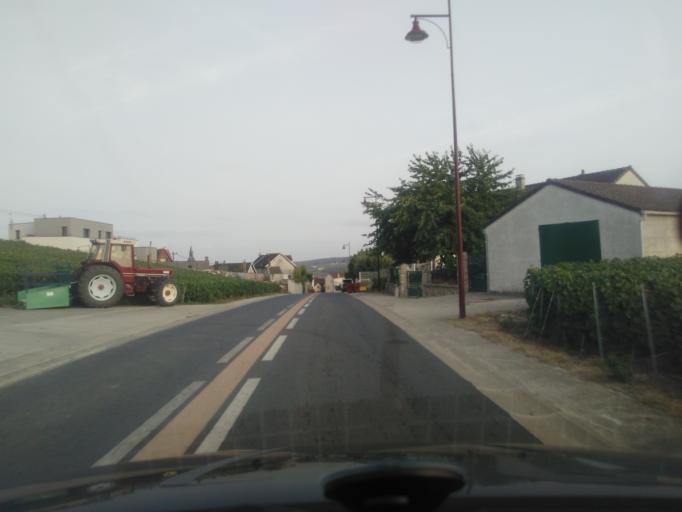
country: FR
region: Champagne-Ardenne
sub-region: Departement de la Marne
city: Damery
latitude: 49.0844
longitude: 3.8371
